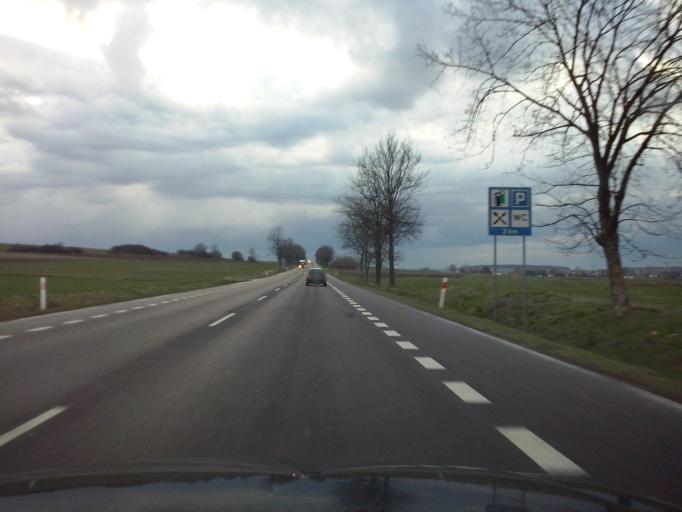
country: PL
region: Lublin Voivodeship
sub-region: Chelm
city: Chelm
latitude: 51.1664
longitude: 23.3689
